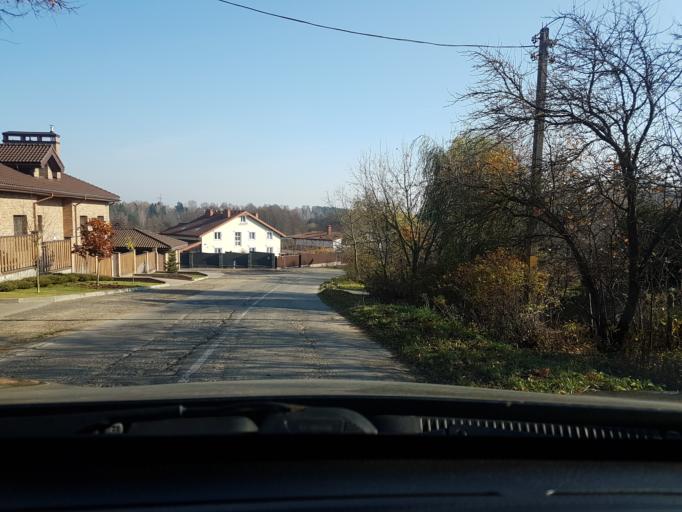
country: BY
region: Minsk
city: Azyartso
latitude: 53.8173
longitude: 27.3645
